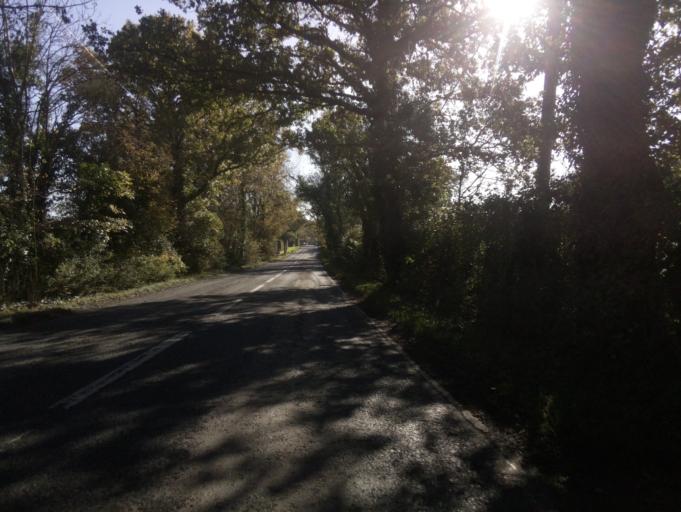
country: GB
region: England
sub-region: Dorset
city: Sherborne
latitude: 50.9007
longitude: -2.4951
